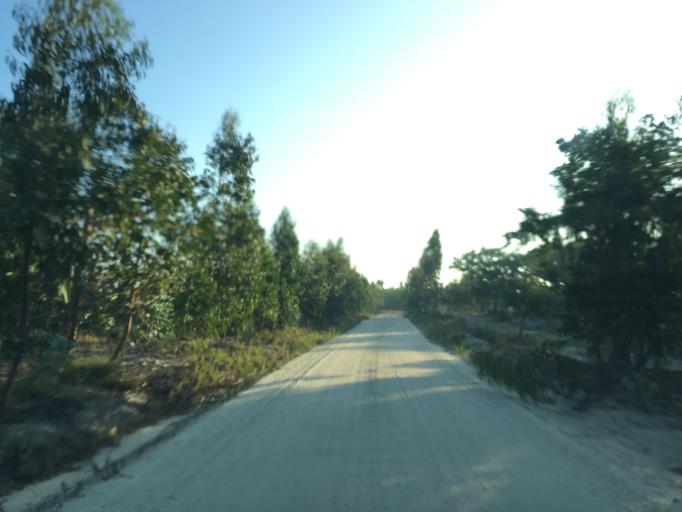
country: PT
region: Portalegre
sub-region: Ponte de Sor
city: Santo Andre
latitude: 39.0741
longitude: -8.3938
